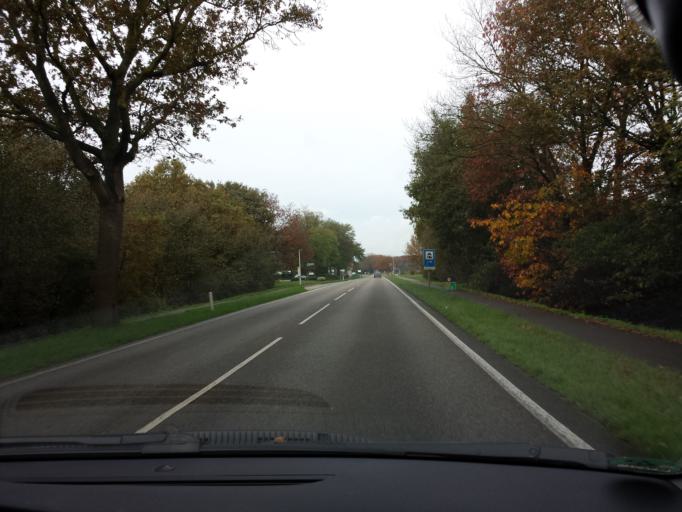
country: NL
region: North Brabant
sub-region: Gemeente Boxmeer
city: Boxmeer
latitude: 51.6420
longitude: 6.0005
